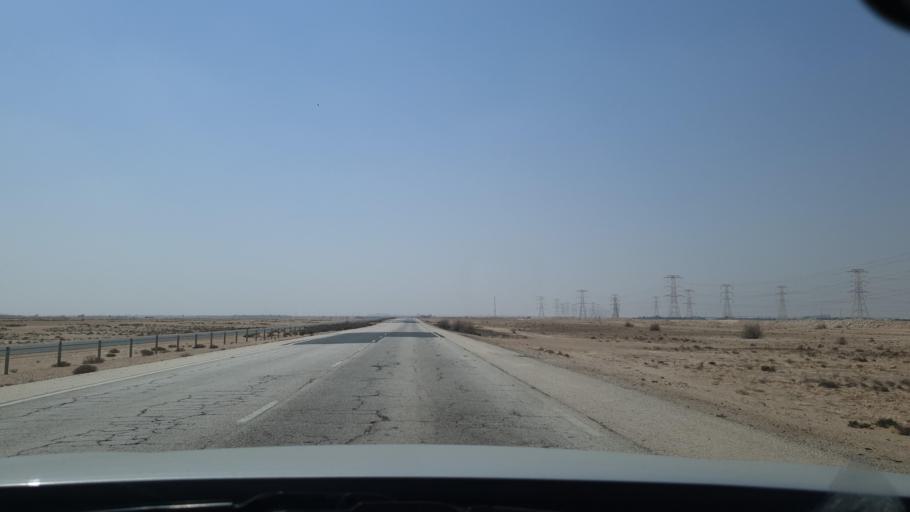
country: QA
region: Al Khawr
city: Al Khawr
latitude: 25.7070
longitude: 51.4461
